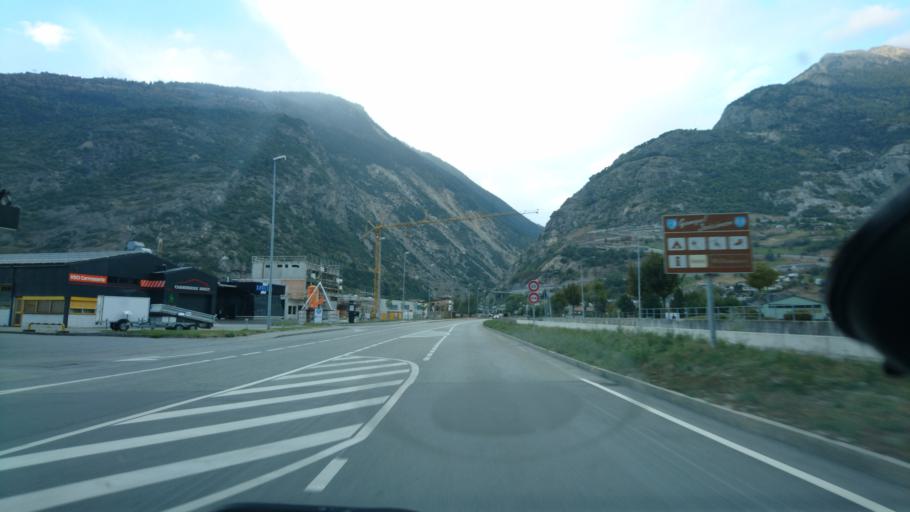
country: CH
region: Valais
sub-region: Leuk District
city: Gampel
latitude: 46.3089
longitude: 7.7447
